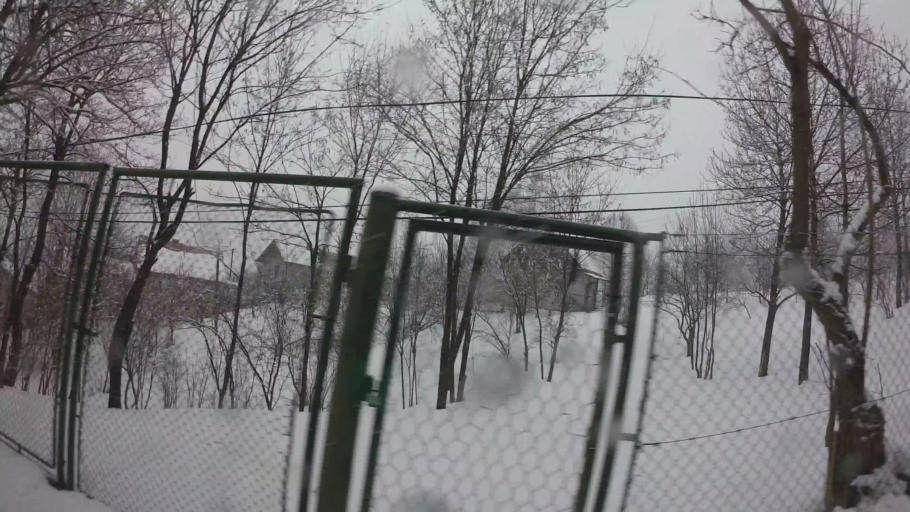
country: BA
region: Federation of Bosnia and Herzegovina
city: Kobilja Glava
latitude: 43.8504
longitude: 18.4378
